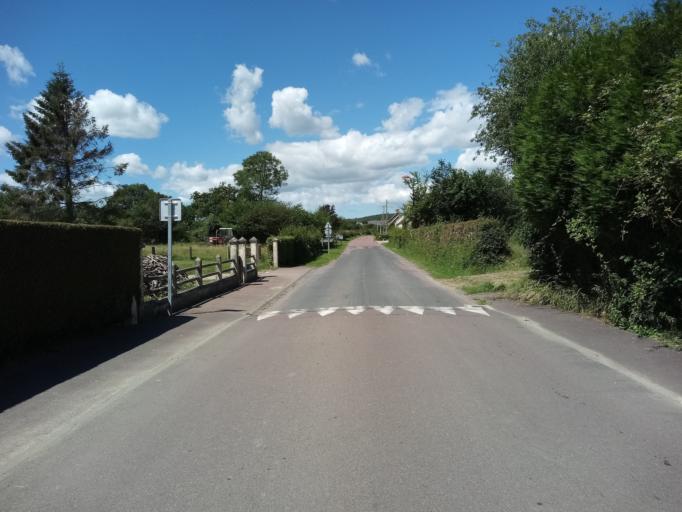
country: FR
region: Lower Normandy
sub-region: Departement de la Manche
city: Periers
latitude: 49.2810
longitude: -1.4265
